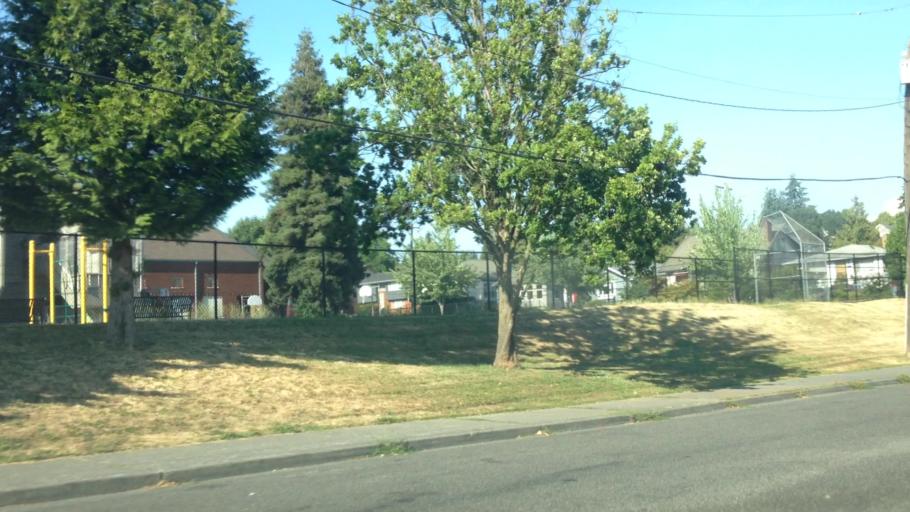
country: US
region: Washington
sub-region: King County
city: Seattle
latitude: 47.5725
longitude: -122.2910
